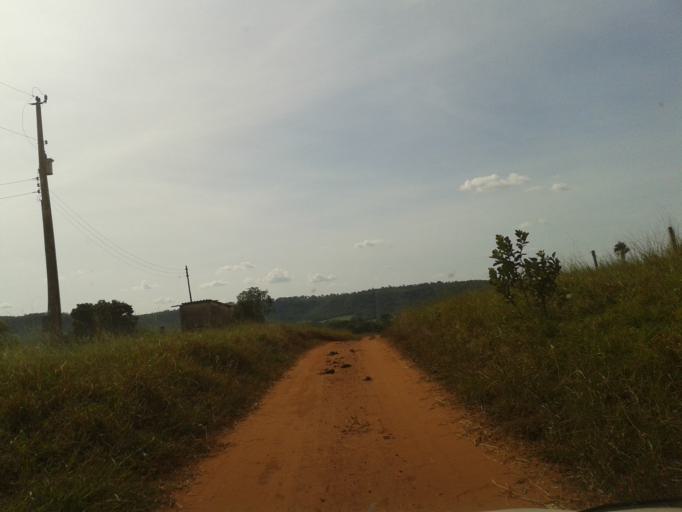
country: BR
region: Minas Gerais
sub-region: Campina Verde
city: Campina Verde
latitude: -19.5091
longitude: -49.5890
